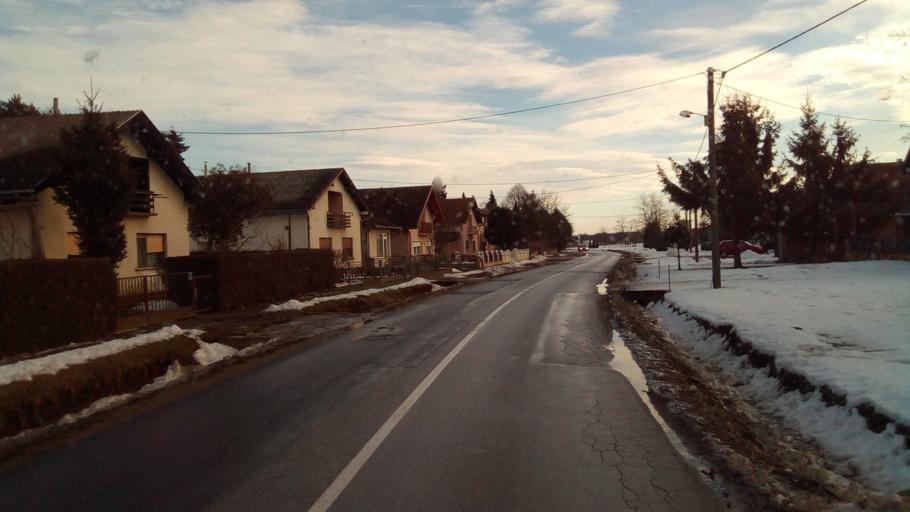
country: HR
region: Medimurska
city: Pribislavec
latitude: 46.3970
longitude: 16.4907
